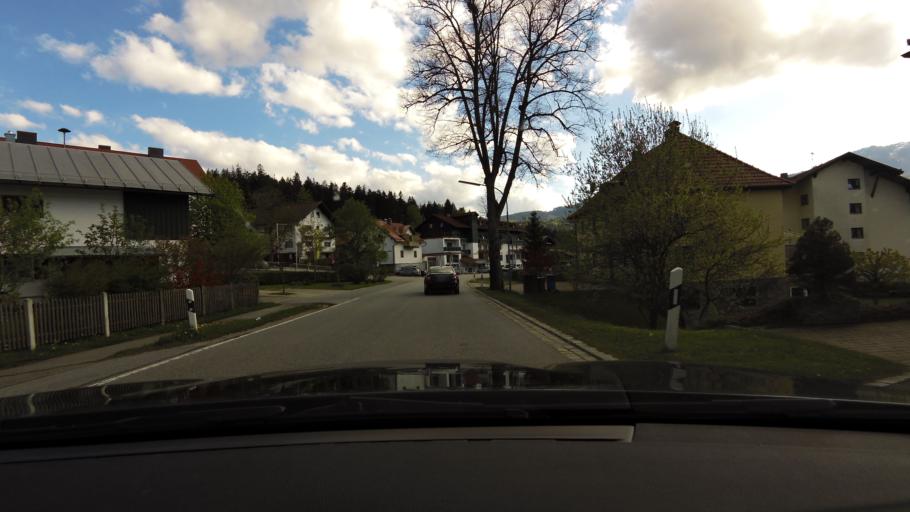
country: DE
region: Bavaria
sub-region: Lower Bavaria
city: Bayerisch Eisenstein
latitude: 49.1203
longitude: 13.1982
